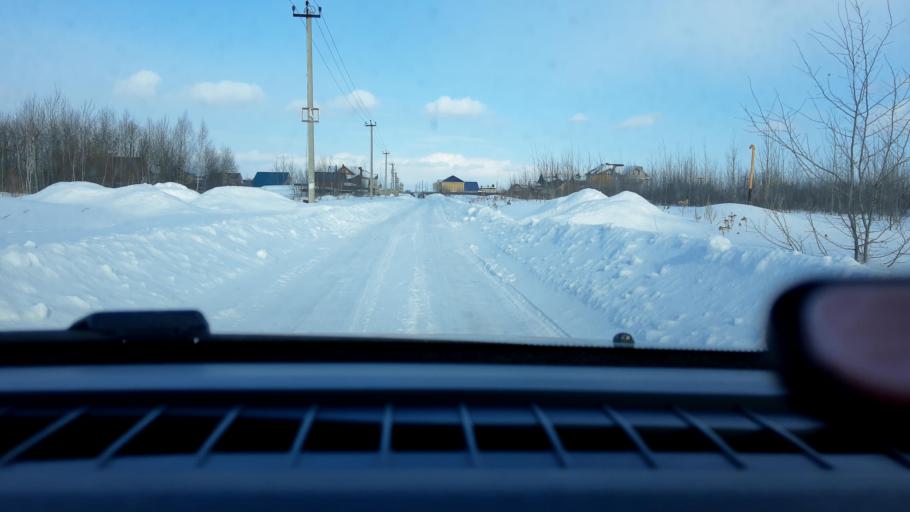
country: RU
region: Nizjnij Novgorod
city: Lukino
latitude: 56.4193
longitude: 43.7192
